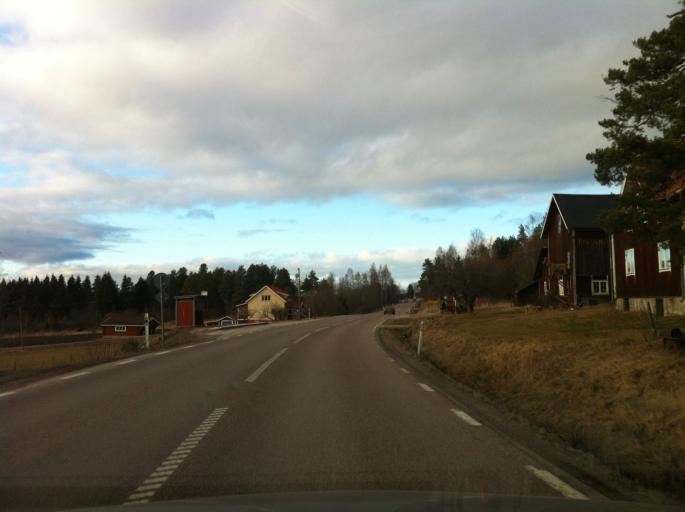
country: SE
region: Dalarna
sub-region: Orsa Kommun
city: Orsa
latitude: 61.0762
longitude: 14.6194
